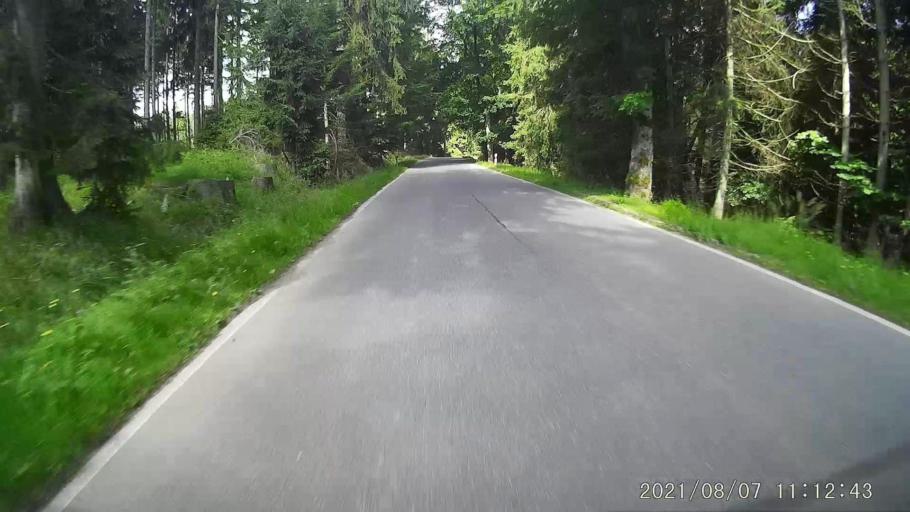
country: CZ
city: Rokytnice v Orlickych Horach
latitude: 50.2749
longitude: 16.5164
